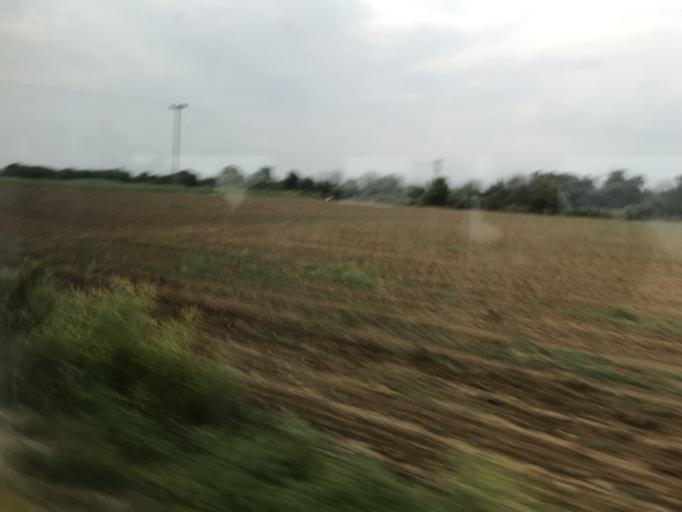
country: GR
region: East Macedonia and Thrace
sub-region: Nomos Rodopis
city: Arisvi
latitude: 41.0458
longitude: 25.6347
